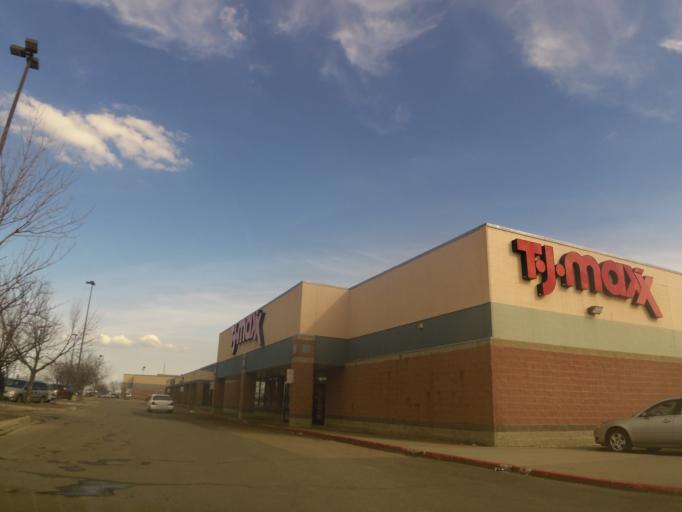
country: US
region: North Dakota
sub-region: Grand Forks County
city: Grand Forks
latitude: 47.8880
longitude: -97.0709
